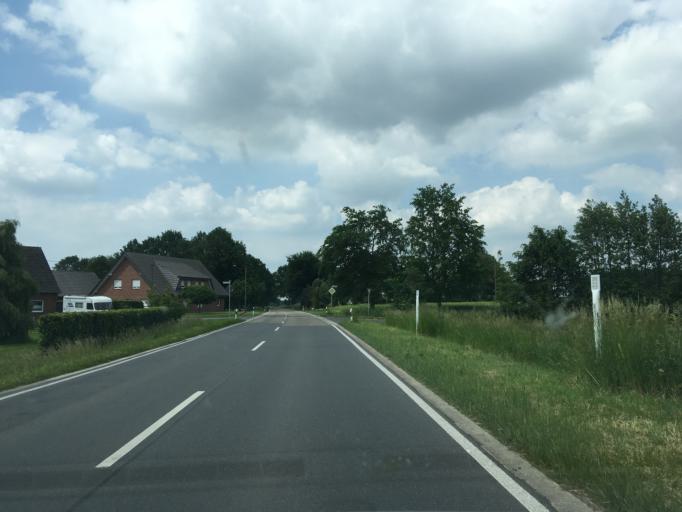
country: DE
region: North Rhine-Westphalia
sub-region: Regierungsbezirk Munster
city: Raesfeld
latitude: 51.7688
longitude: 6.8164
